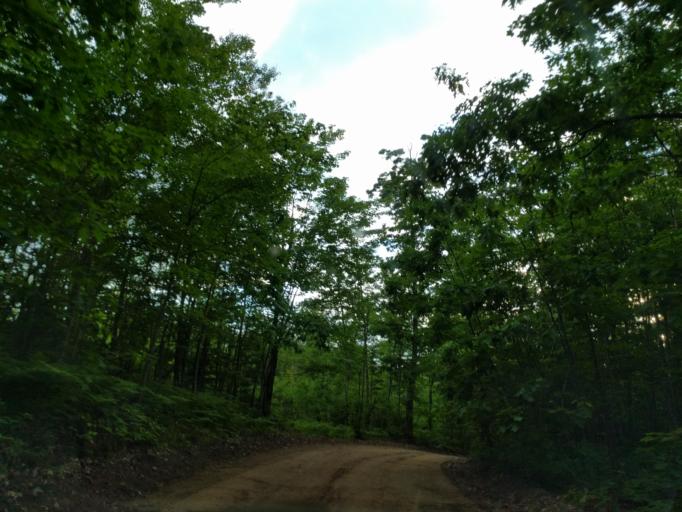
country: US
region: Michigan
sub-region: Marquette County
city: Trowbridge Park
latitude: 46.6121
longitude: -87.5099
